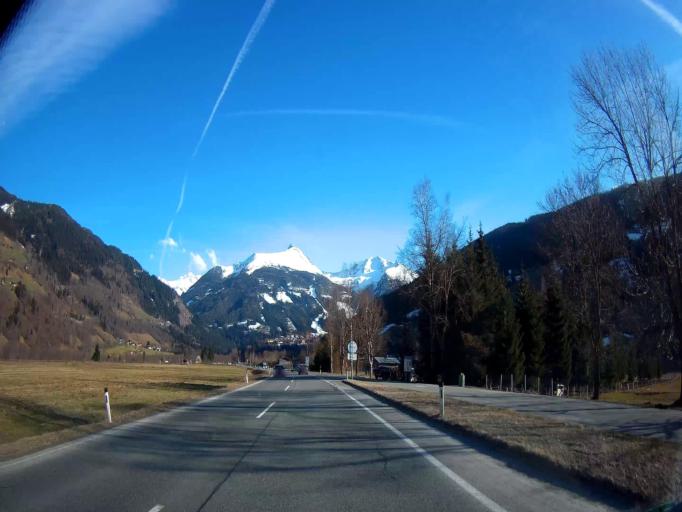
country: AT
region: Salzburg
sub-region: Politischer Bezirk Sankt Johann im Pongau
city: Bad Hofgastein
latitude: 47.1477
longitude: 13.1151
